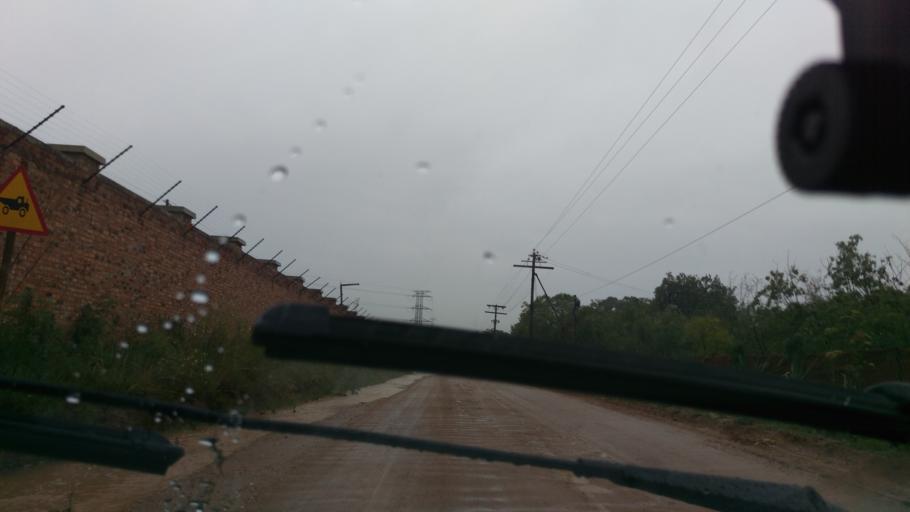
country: ZA
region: Gauteng
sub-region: City of Johannesburg Metropolitan Municipality
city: Diepsloot
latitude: -25.9668
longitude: 27.9759
